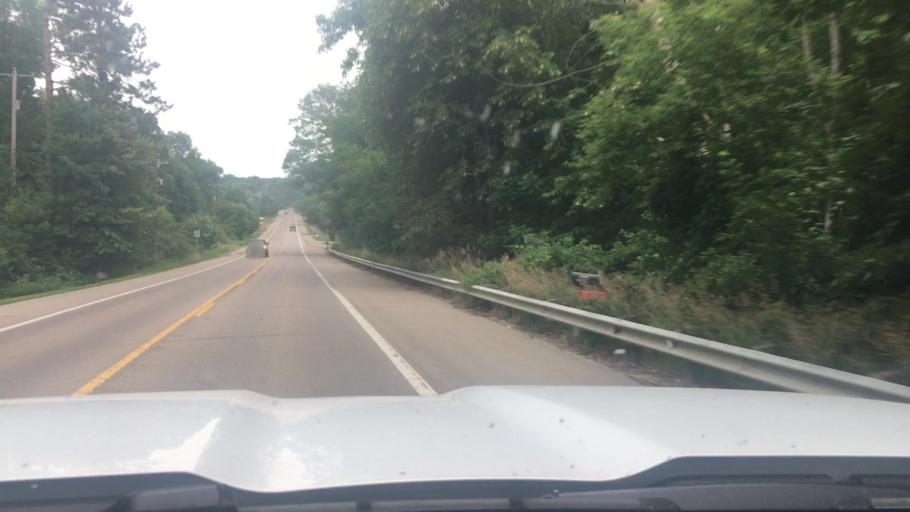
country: US
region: Michigan
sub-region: Ionia County
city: Ionia
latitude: 42.9991
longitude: -85.0192
